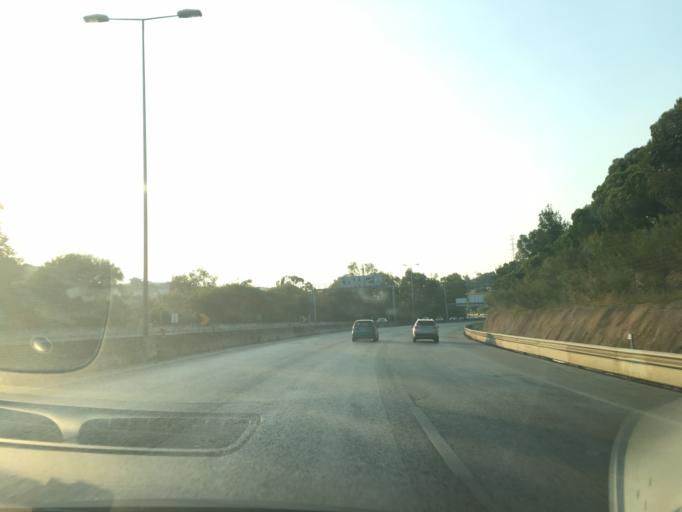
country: PT
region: Lisbon
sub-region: Sintra
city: Cacem
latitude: 38.7533
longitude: -9.2895
